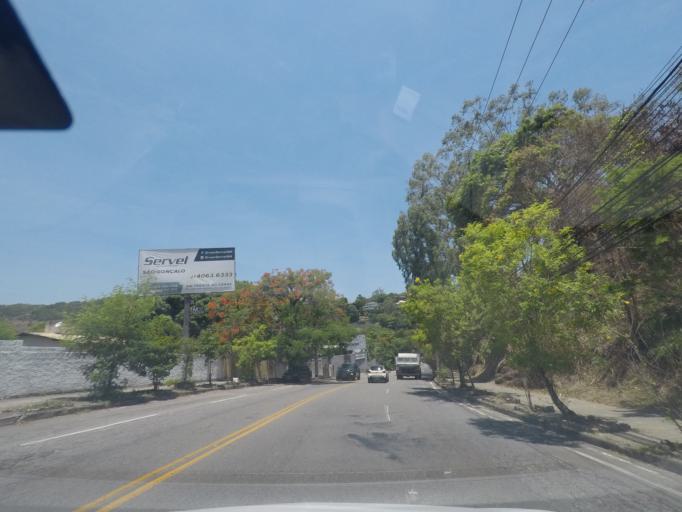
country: BR
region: Rio de Janeiro
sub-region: Niteroi
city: Niteroi
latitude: -22.9132
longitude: -43.0666
